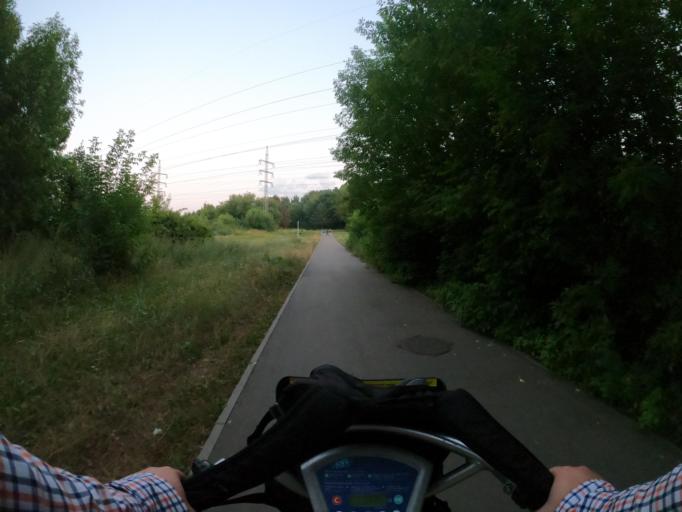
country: RU
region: Moscow
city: Lyublino
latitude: 55.6876
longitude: 37.7614
